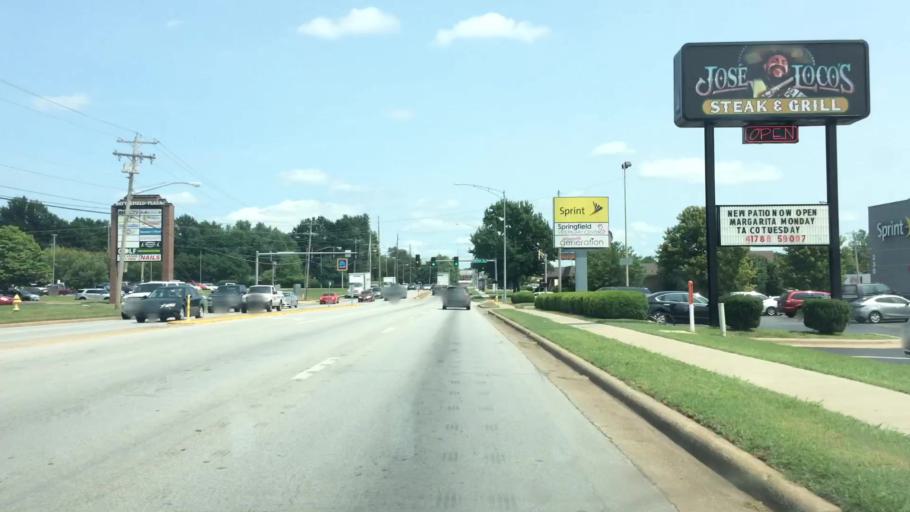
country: US
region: Missouri
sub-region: Greene County
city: Springfield
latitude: 37.1599
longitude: -93.2923
